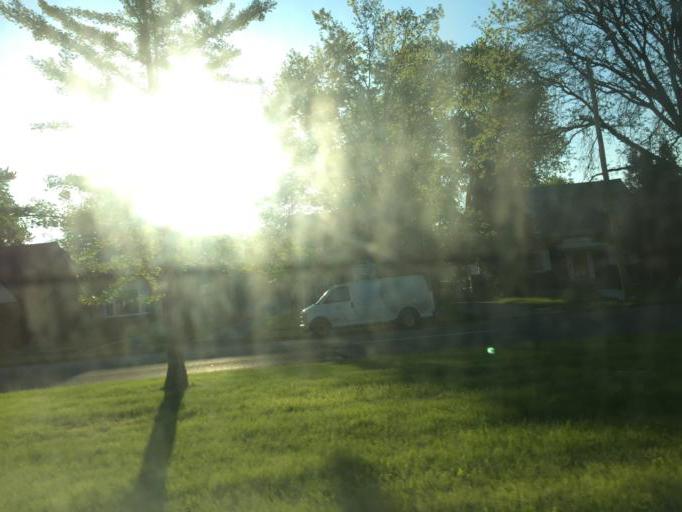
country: US
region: Michigan
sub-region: Wayne County
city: Redford
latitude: 42.4053
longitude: -83.2329
